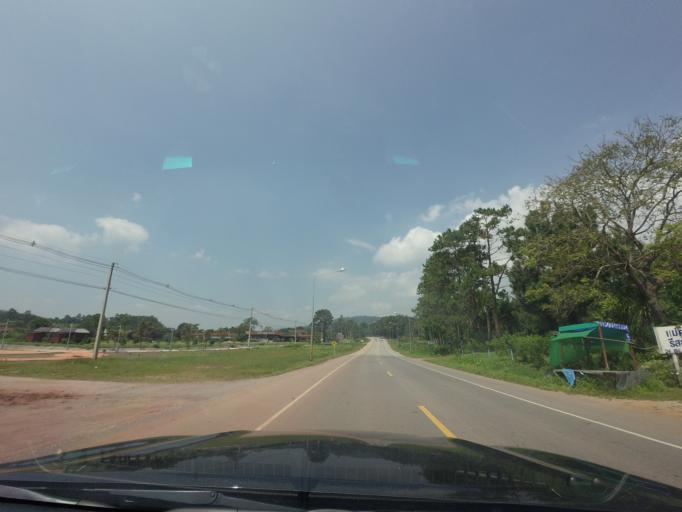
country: TH
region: Loei
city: Phu Ruea
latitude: 17.4575
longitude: 101.3881
